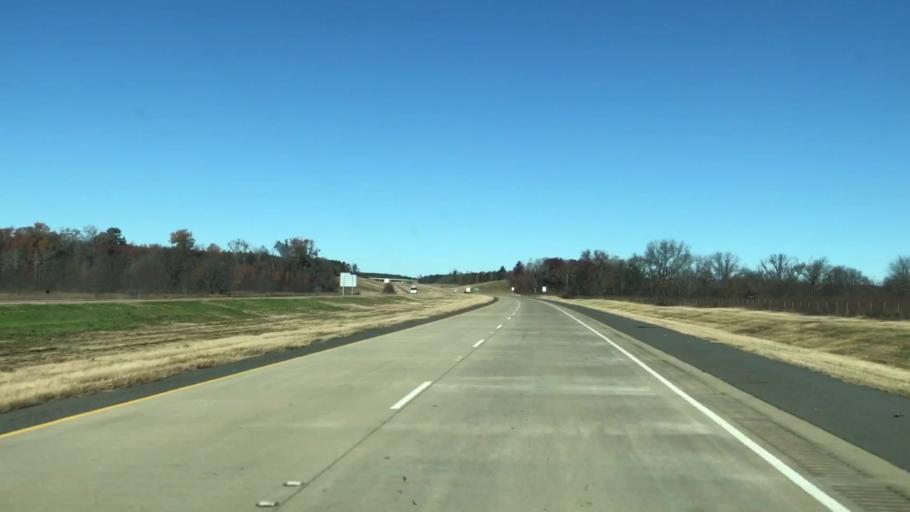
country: US
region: Louisiana
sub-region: Caddo Parish
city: Vivian
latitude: 32.9074
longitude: -93.8673
